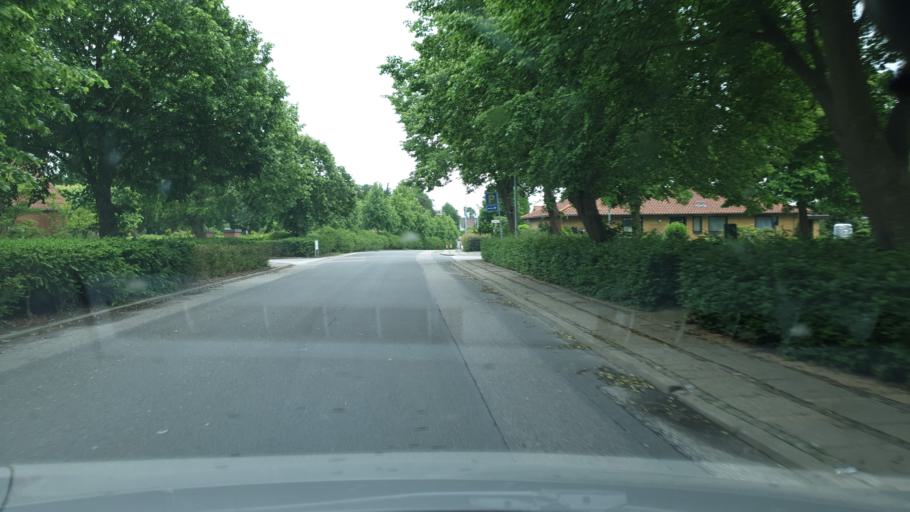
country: DK
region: South Denmark
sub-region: Kolding Kommune
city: Kolding
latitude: 55.4790
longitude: 9.4779
